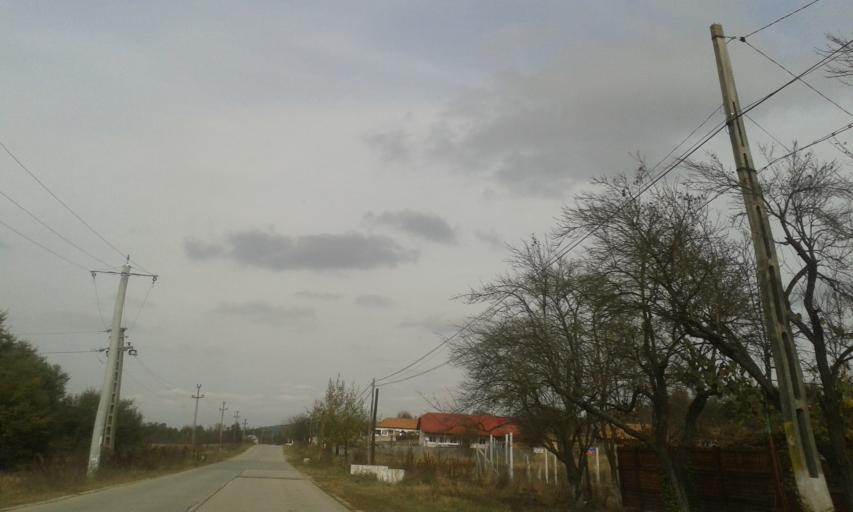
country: RO
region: Gorj
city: Logresti
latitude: 44.8631
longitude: 23.7011
